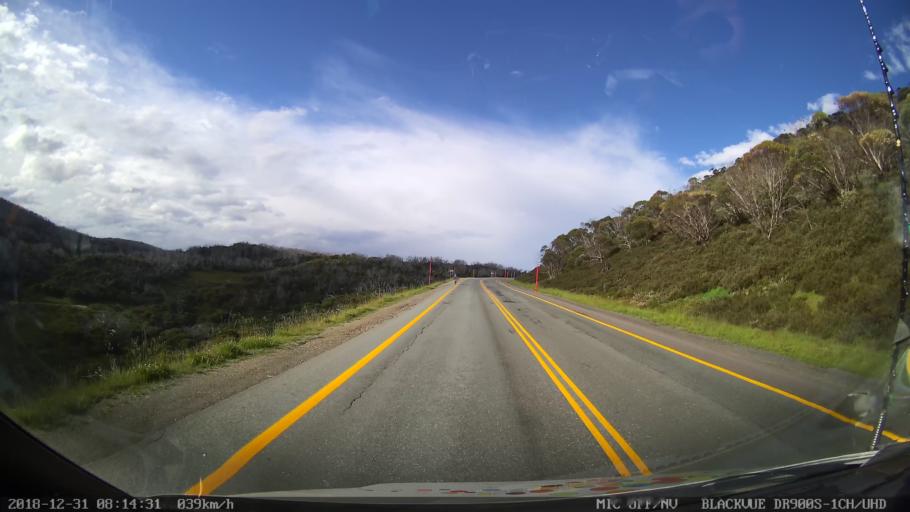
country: AU
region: New South Wales
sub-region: Snowy River
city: Jindabyne
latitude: -36.3956
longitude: 148.4259
